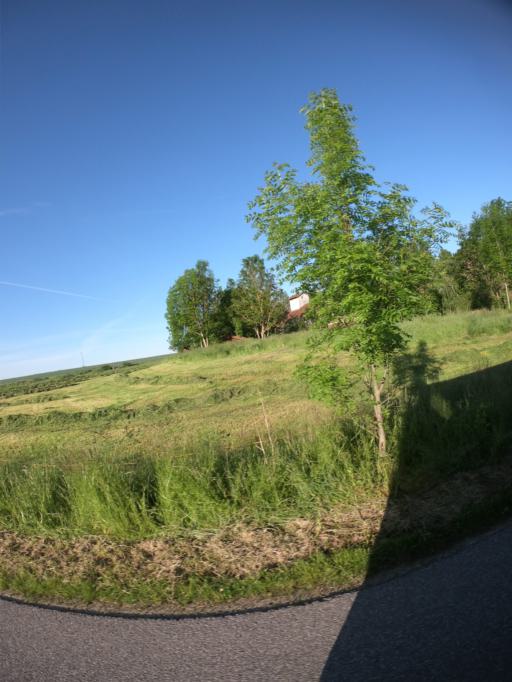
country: DE
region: Bavaria
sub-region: Upper Bavaria
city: Bockhorn
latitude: 48.3049
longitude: 11.9613
